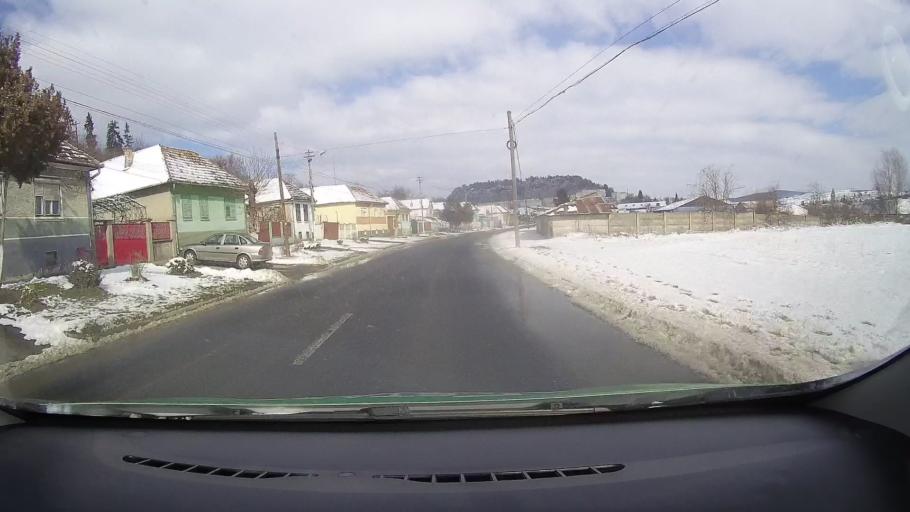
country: RO
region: Sibiu
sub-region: Oras Agnita
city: Agnita
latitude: 45.9740
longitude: 24.6101
